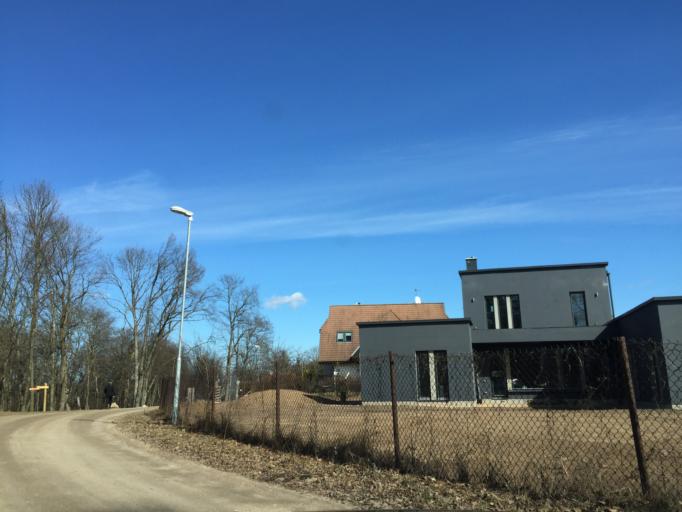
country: LV
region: Sigulda
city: Sigulda
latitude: 57.1423
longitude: 24.8240
